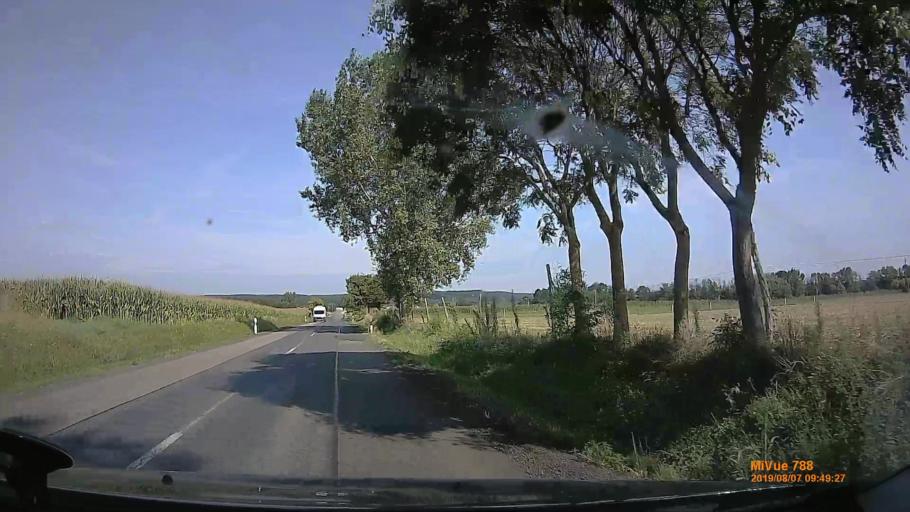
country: HU
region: Zala
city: Pacsa
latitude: 46.7379
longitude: 16.9346
